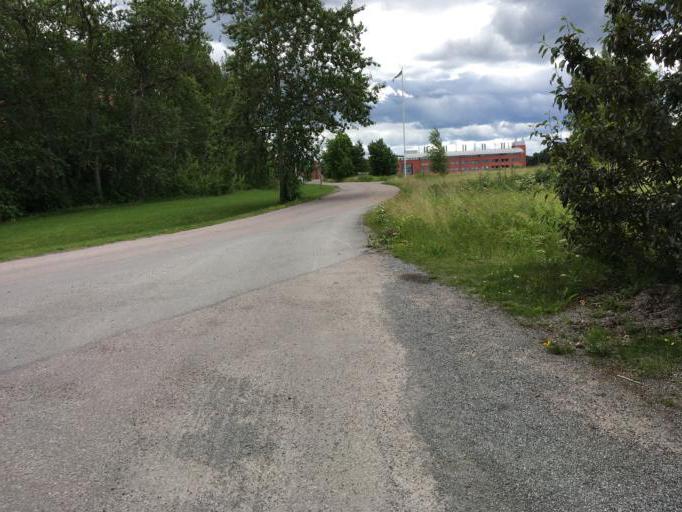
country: SE
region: Uppsala
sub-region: Uppsala Kommun
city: Uppsala
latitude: 59.8425
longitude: 17.6467
